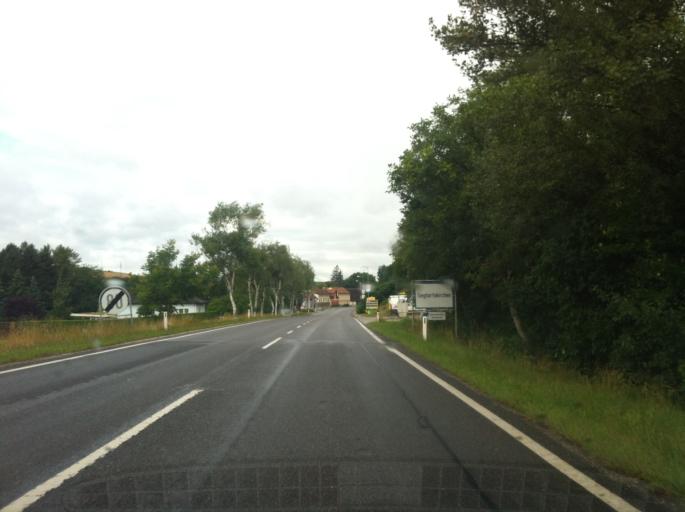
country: AT
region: Lower Austria
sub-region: Politischer Bezirk Tulln
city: Sieghartskirchen
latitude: 48.2537
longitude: 16.0213
